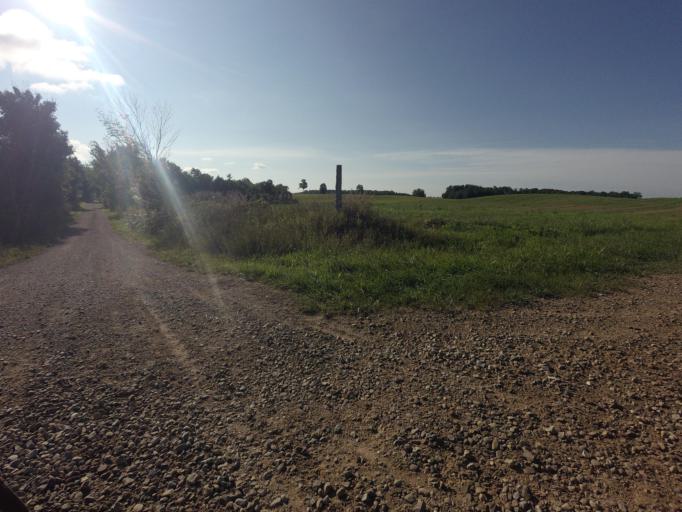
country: CA
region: Ontario
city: Huron East
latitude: 43.7405
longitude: -81.4749
